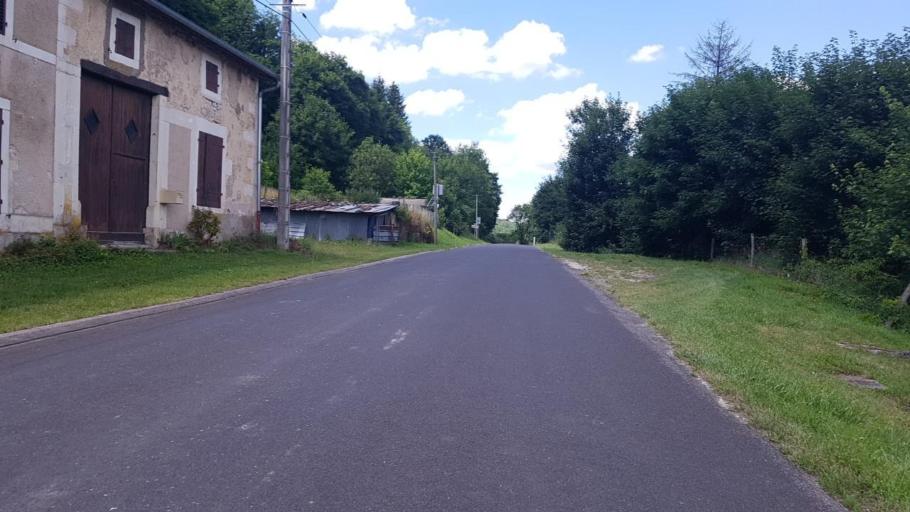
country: FR
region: Lorraine
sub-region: Departement de la Meuse
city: Gondrecourt-le-Chateau
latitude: 48.6306
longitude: 5.4653
